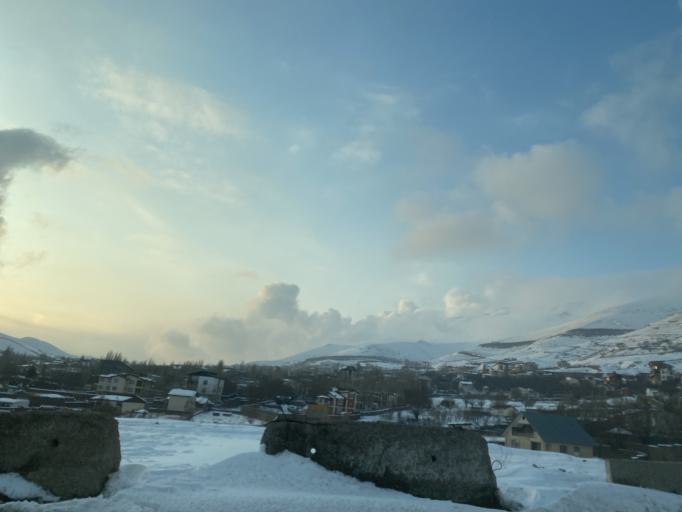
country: IR
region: Tehran
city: Damavand
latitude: 35.7683
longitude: 52.0274
